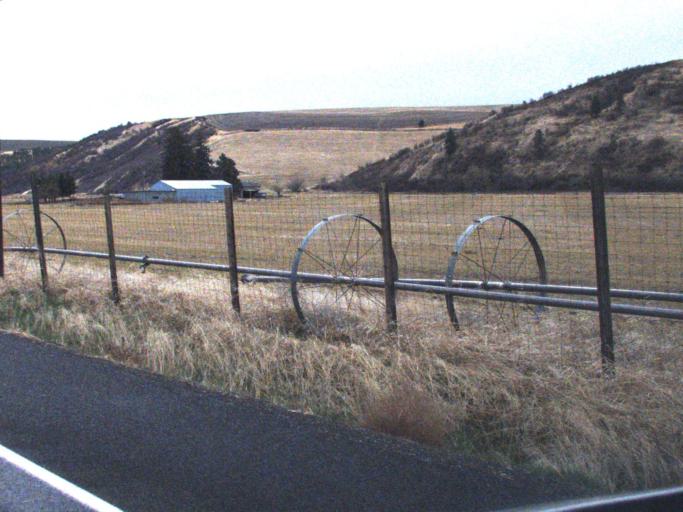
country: US
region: Washington
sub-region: Walla Walla County
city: Waitsburg
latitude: 46.2868
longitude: -118.0631
